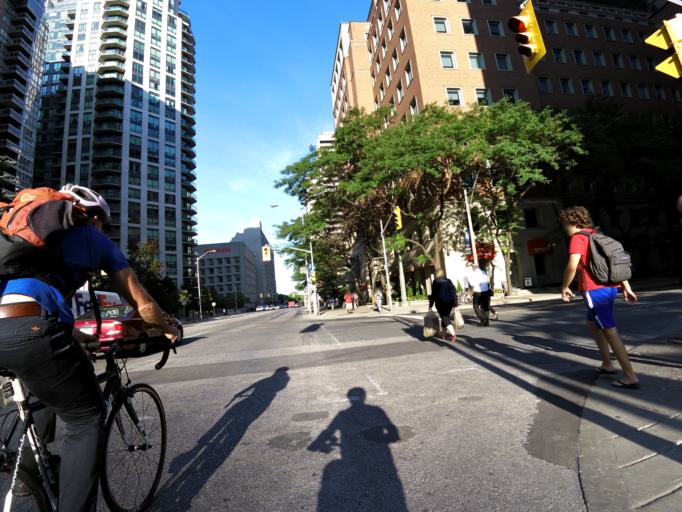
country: CA
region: Ontario
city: Toronto
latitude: 43.6724
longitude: -79.3810
